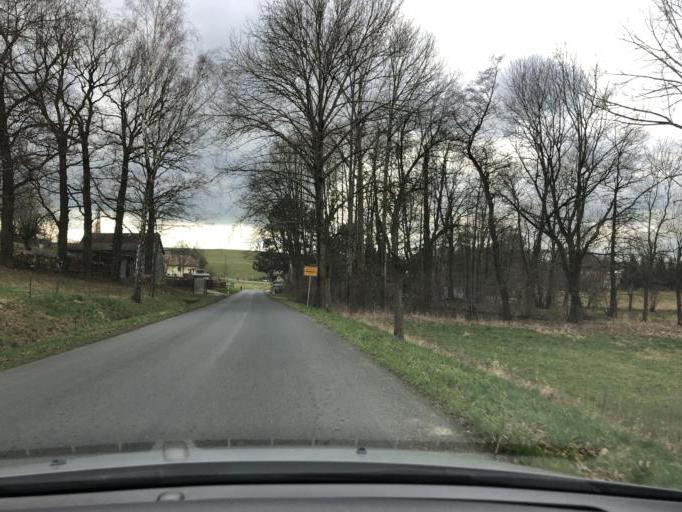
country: DE
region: Saxony
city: Bockelwitz
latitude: 51.2011
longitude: 12.9274
